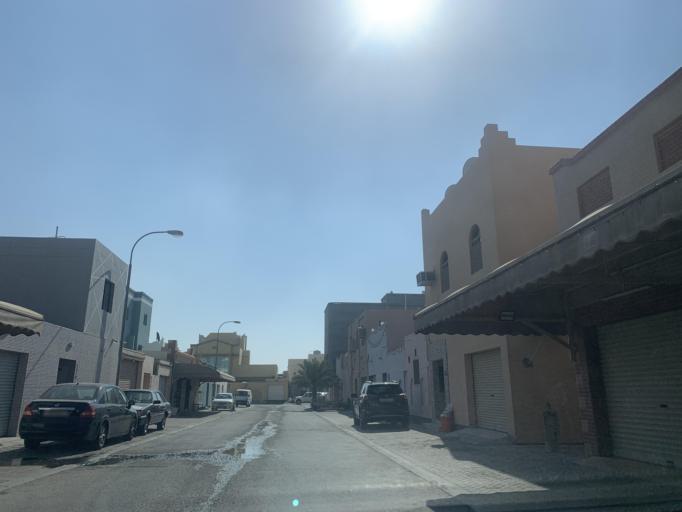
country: BH
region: Central Governorate
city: Madinat Hamad
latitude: 26.1226
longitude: 50.4953
